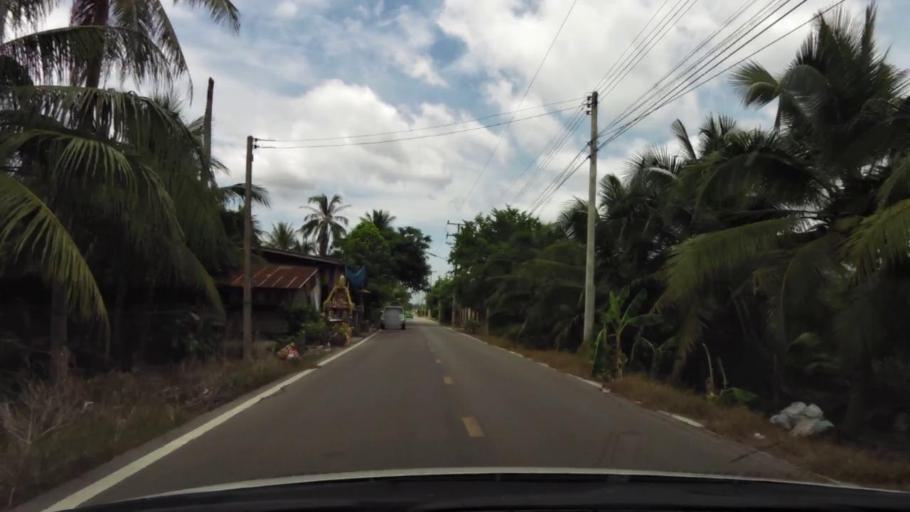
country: TH
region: Ratchaburi
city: Damnoen Saduak
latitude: 13.5220
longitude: 100.0101
